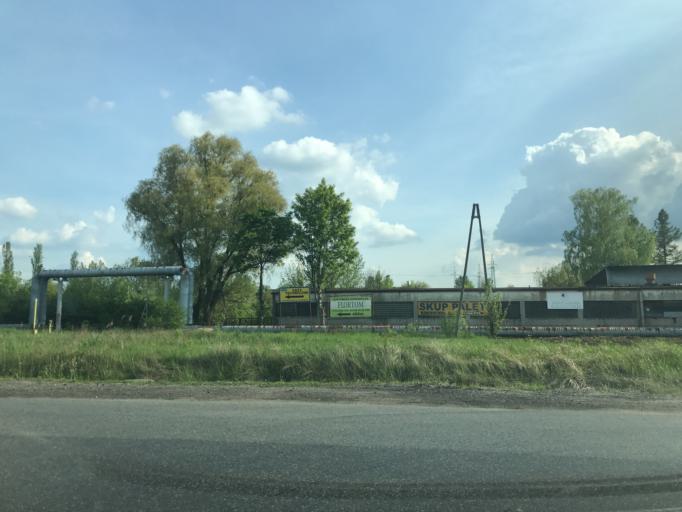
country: PL
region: Kujawsko-Pomorskie
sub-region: Powiat bydgoski
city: Osielsko
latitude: 53.1183
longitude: 18.0873
